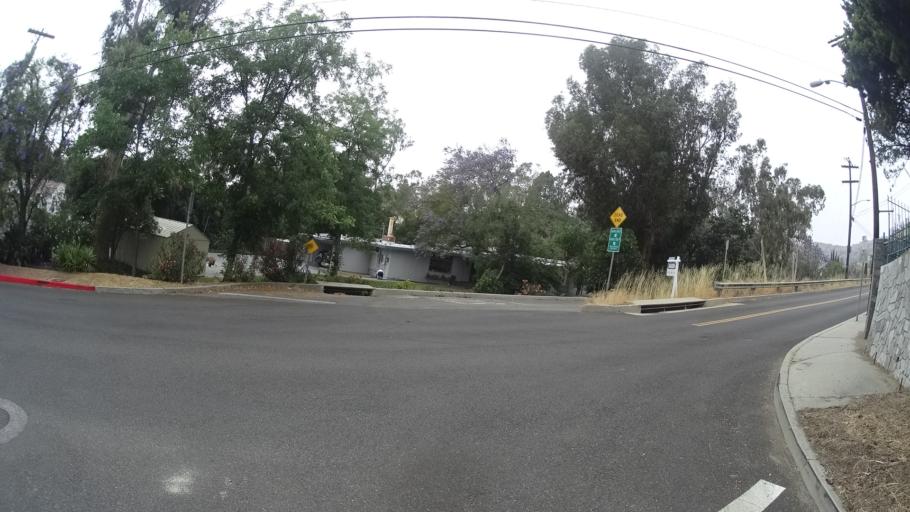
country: US
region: California
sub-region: Los Angeles County
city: Burbank
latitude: 34.1934
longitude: -118.2958
